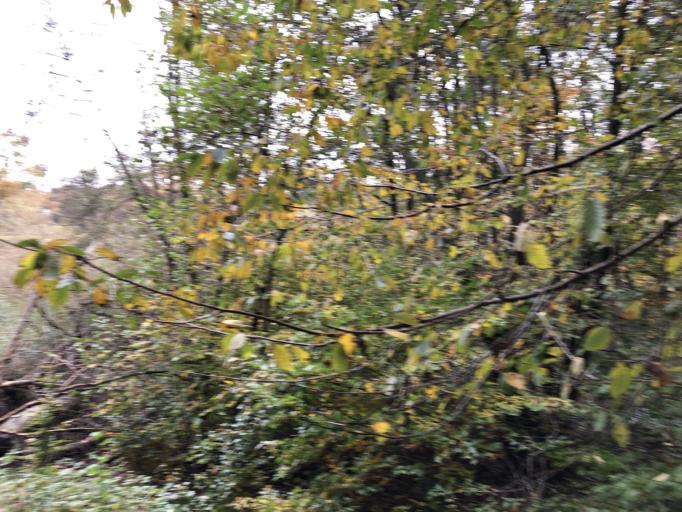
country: DK
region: Capital Region
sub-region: Lyngby-Tarbaek Kommune
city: Kongens Lyngby
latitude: 55.8009
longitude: 12.5098
